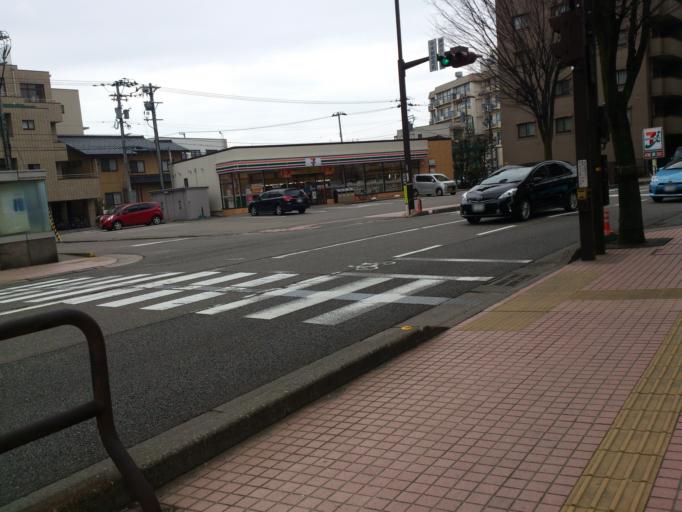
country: JP
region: Ishikawa
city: Kanazawa-shi
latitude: 36.5714
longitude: 136.6461
